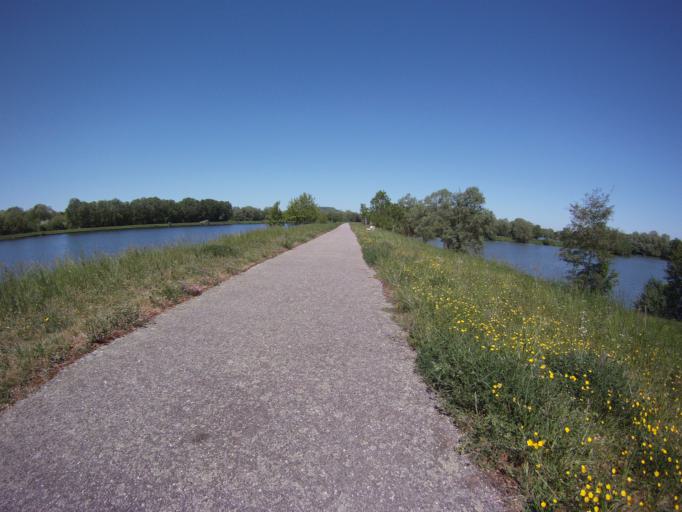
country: FR
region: Lorraine
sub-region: Departement de Meurthe-et-Moselle
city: Dommartin-les-Toul
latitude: 48.6621
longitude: 5.8944
